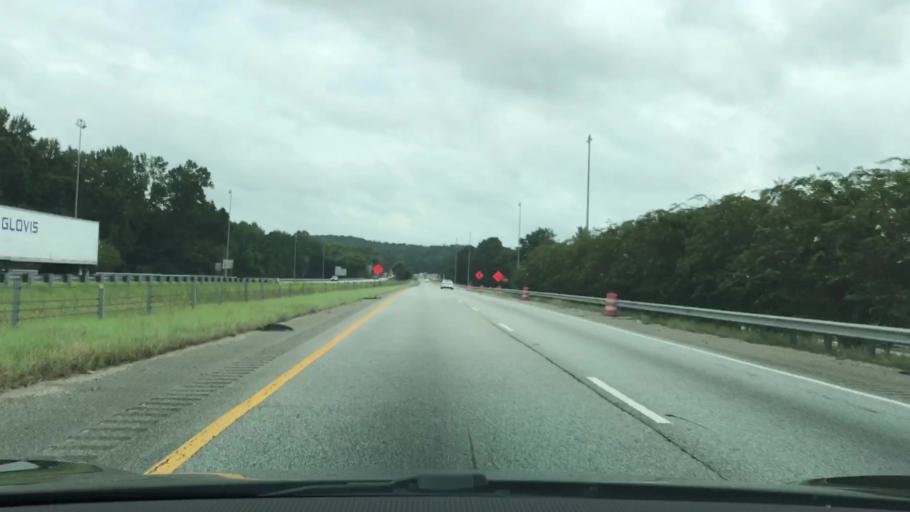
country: US
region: Alabama
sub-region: Macon County
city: Tuskegee
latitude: 32.4729
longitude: -85.6917
